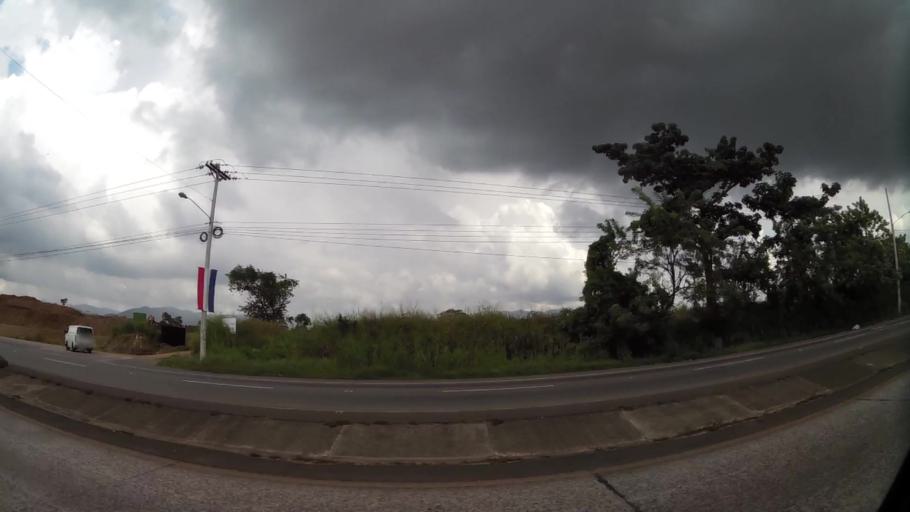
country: PA
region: Panama
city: Cabra Numero Uno
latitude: 9.1010
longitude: -79.3388
